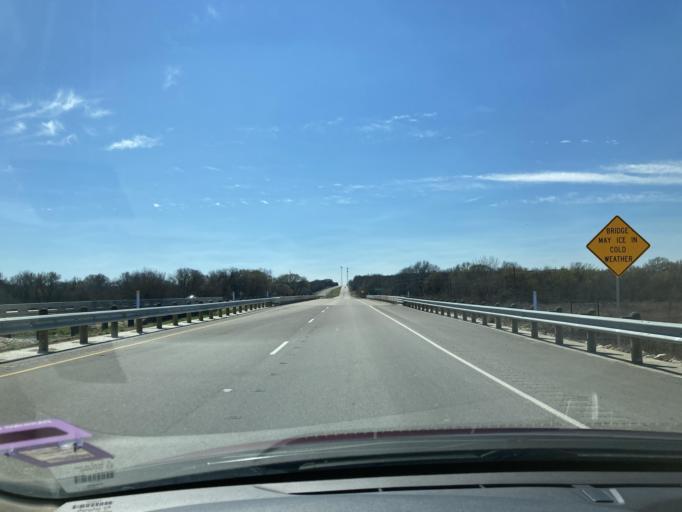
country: US
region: Texas
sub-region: Navarro County
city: Corsicana
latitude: 32.1493
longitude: -96.4681
